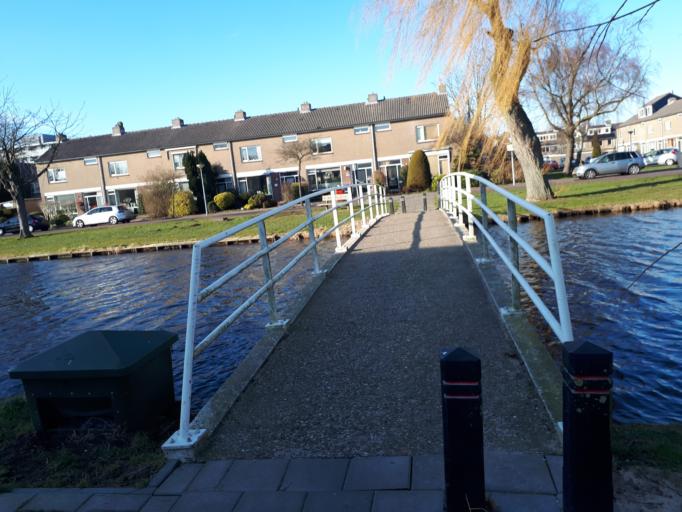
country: NL
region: North Holland
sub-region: Gemeente Zaanstad
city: Zaanstad
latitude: 52.4710
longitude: 4.7999
